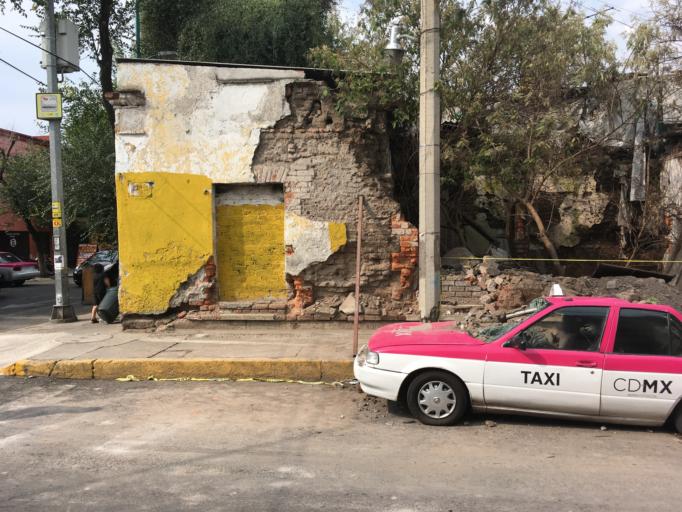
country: MX
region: Mexico City
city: Cuauhtemoc
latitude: 19.4477
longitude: -99.1419
